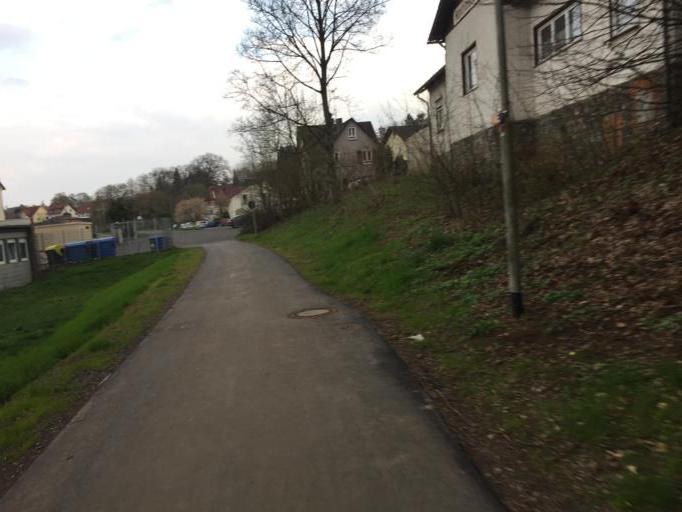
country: DE
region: Hesse
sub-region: Regierungsbezirk Giessen
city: Laubach
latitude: 50.5393
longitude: 8.9874
